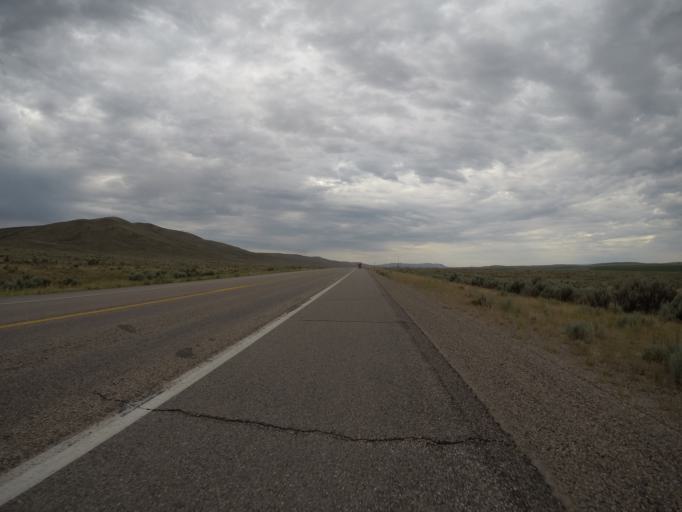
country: US
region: Utah
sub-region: Rich County
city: Randolph
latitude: 41.8618
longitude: -110.9706
